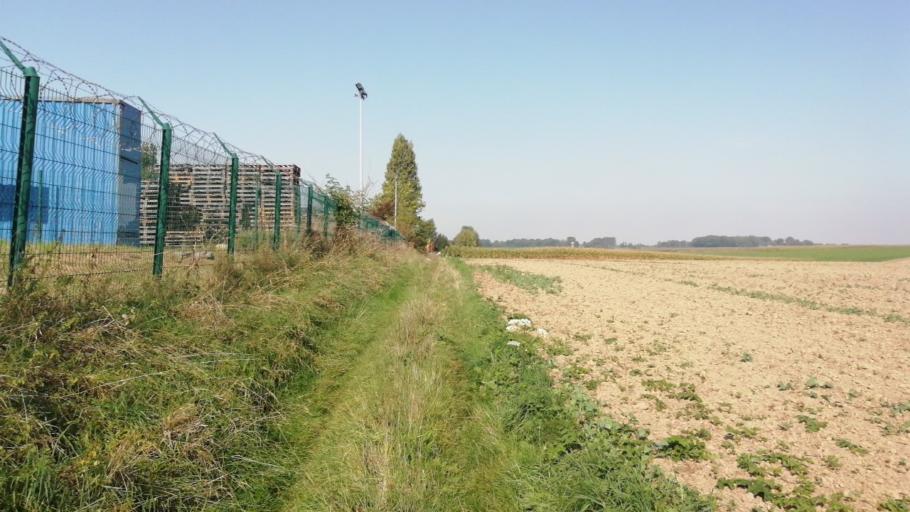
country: FR
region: Haute-Normandie
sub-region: Departement de la Seine-Maritime
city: Saint-Romain-de-Colbosc
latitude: 49.5367
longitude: 0.3599
